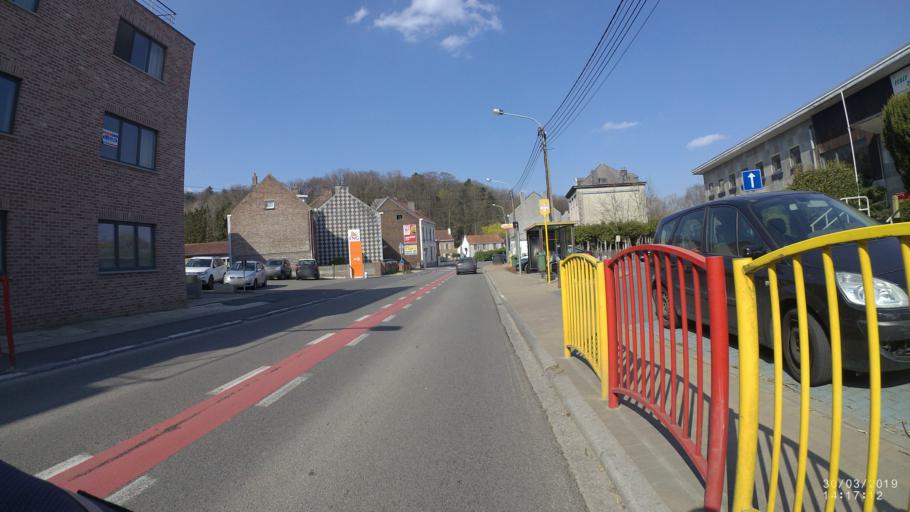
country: BE
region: Wallonia
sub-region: Province du Brabant Wallon
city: Ottignies
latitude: 50.6956
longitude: 4.5754
